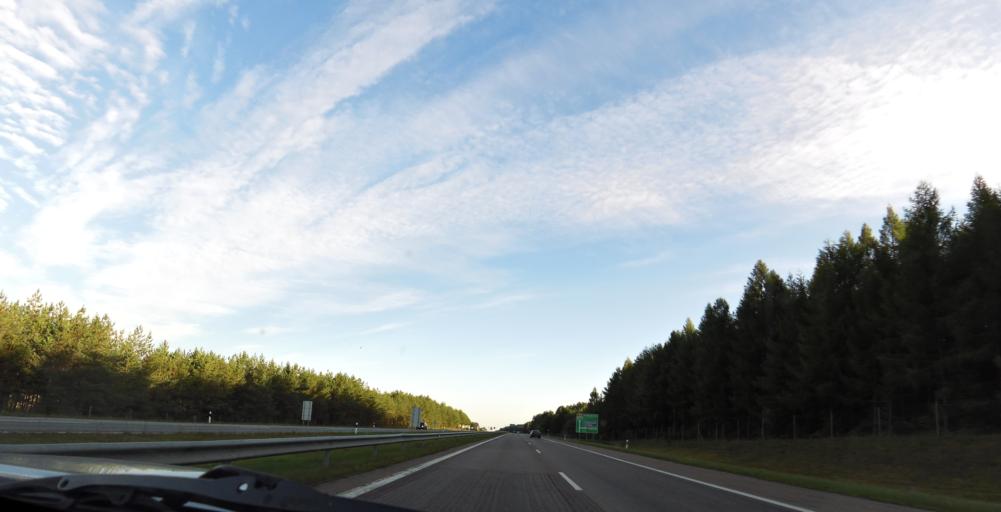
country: LT
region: Vilnius County
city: Ukmerge
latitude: 55.2631
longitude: 24.8137
